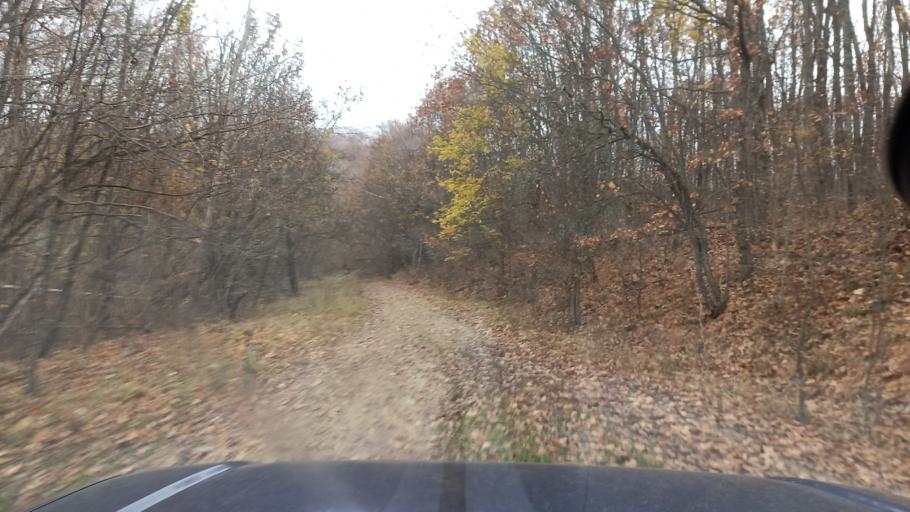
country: RU
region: Krasnodarskiy
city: Goryachiy Klyuch
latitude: 44.4969
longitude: 39.2771
